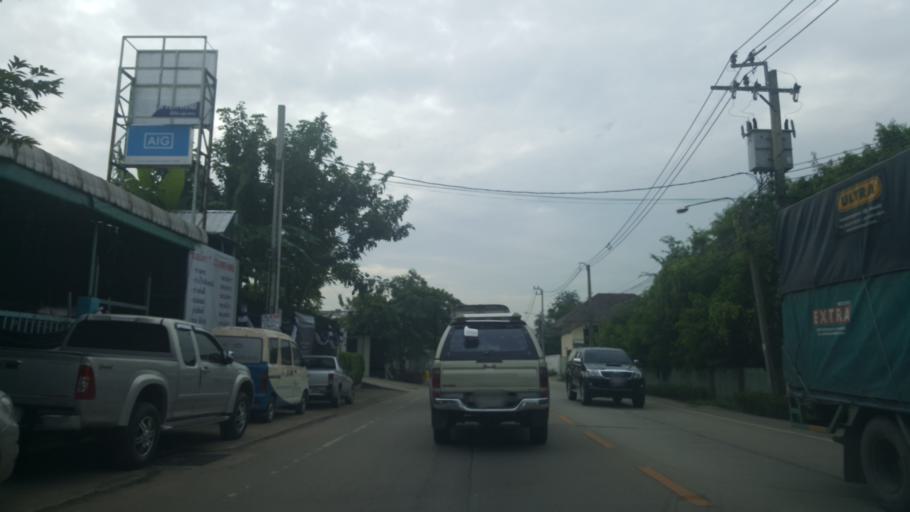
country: TH
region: Bangkok
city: Bang Bon
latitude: 13.6730
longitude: 100.4027
